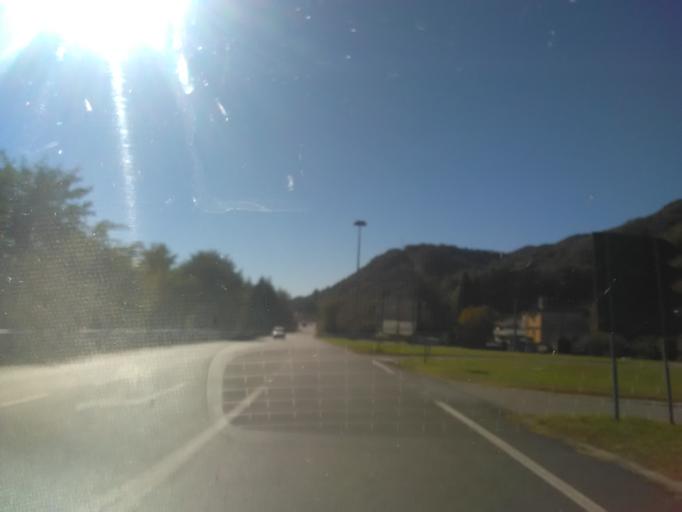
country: IT
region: Piedmont
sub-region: Provincia di Vercelli
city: Quarona
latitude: 45.7678
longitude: 8.2605
